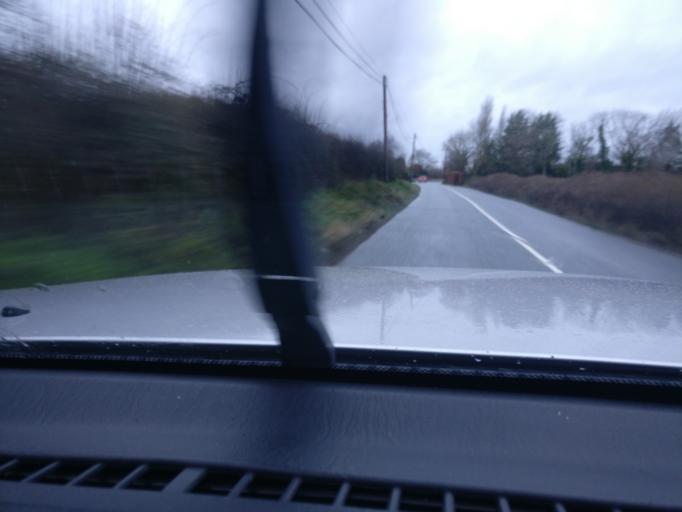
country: IE
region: Leinster
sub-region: An Mhi
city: Trim
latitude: 53.5429
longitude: -6.8023
